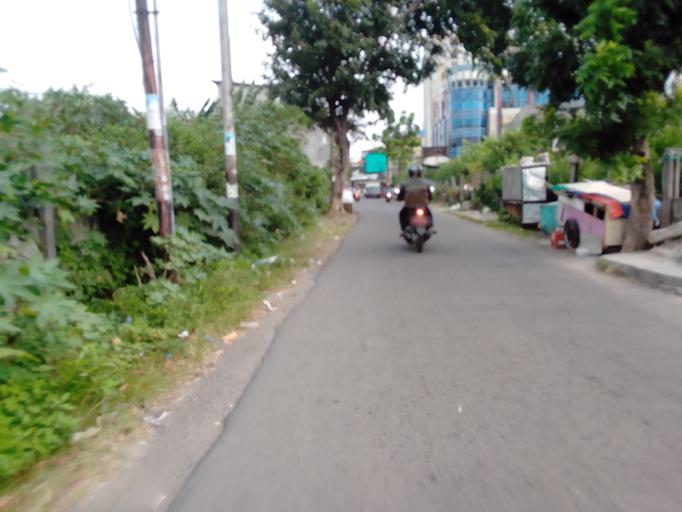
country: ID
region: Jakarta Raya
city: Jakarta
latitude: -6.1650
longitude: 106.8036
